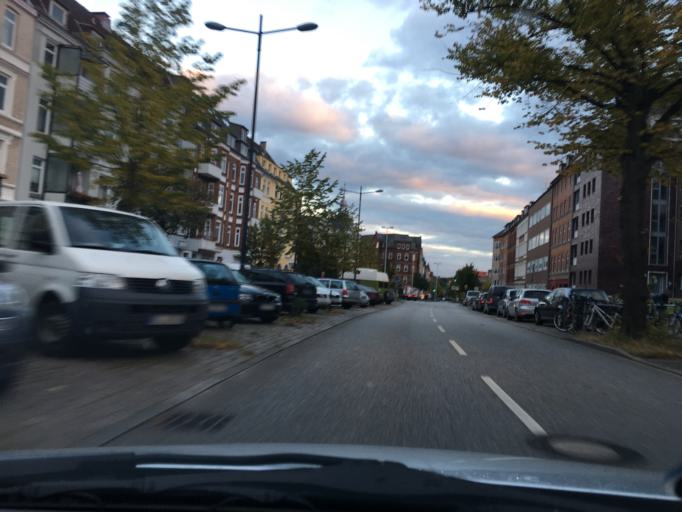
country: DE
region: Schleswig-Holstein
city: Kiel
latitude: 54.3262
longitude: 10.1203
